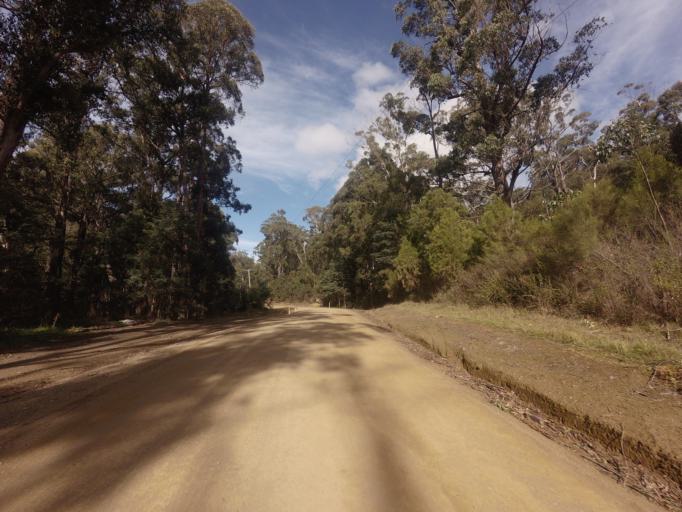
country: AU
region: Tasmania
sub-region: Clarence
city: Sandford
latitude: -43.1239
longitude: 147.7621
